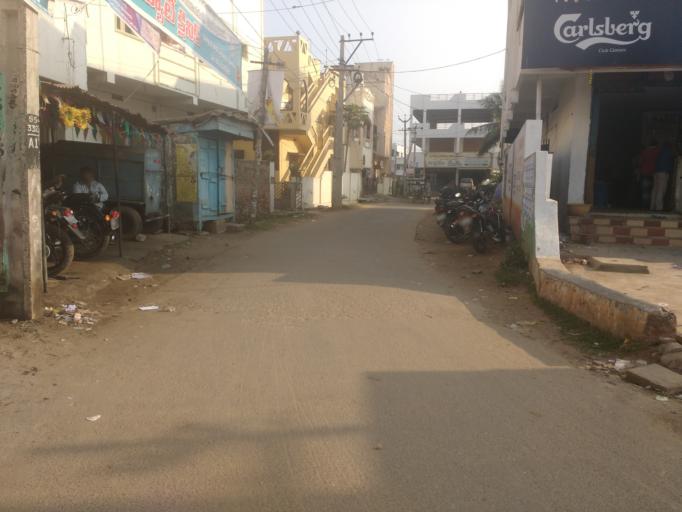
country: IN
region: Andhra Pradesh
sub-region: Srikakulam
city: Srikakulam
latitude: 18.3003
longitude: 83.9062
